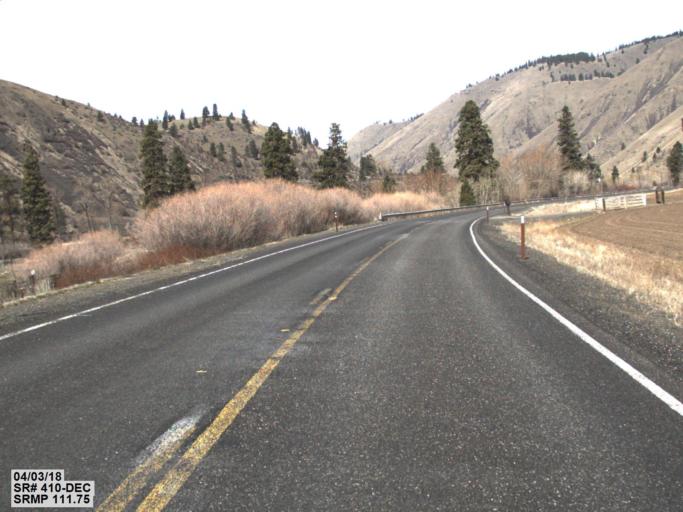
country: US
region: Washington
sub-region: Yakima County
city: Tieton
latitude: 46.7805
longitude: -120.8637
